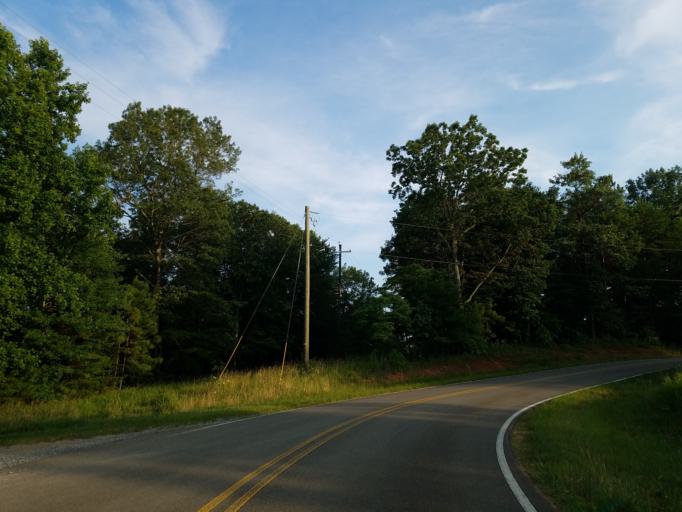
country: US
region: Georgia
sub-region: Pickens County
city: Jasper
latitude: 34.4974
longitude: -84.4195
